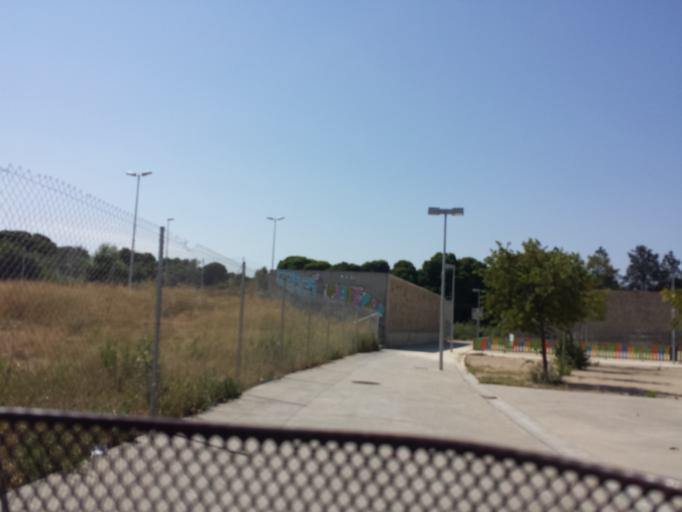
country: ES
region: Aragon
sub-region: Provincia de Zaragoza
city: Oliver-Valdefierro, Oliver, Valdefierro
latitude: 41.6360
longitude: -0.9291
